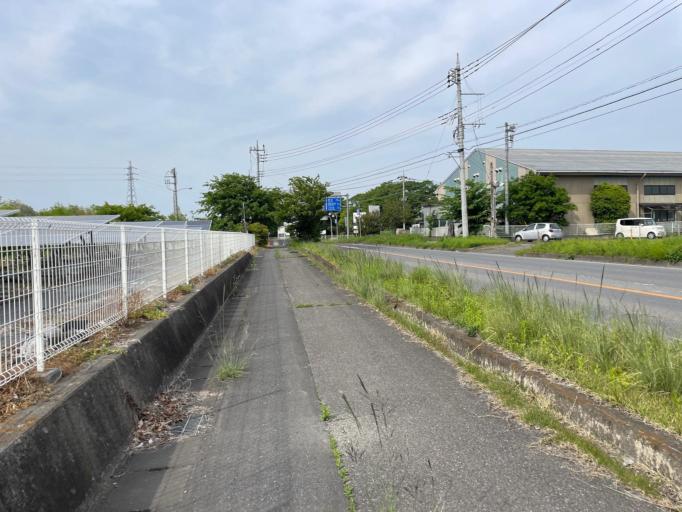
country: JP
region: Tochigi
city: Mibu
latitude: 36.4070
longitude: 139.8046
